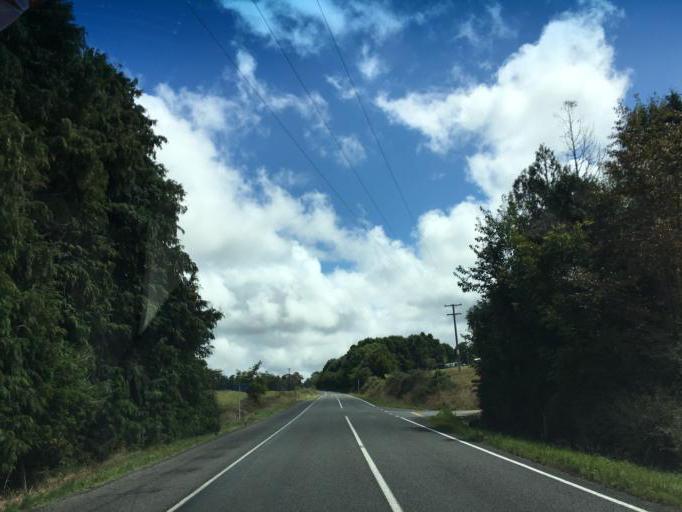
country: NZ
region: Hawke's Bay
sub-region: Wairoa District
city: Wairoa
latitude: -39.0631
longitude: 177.0344
